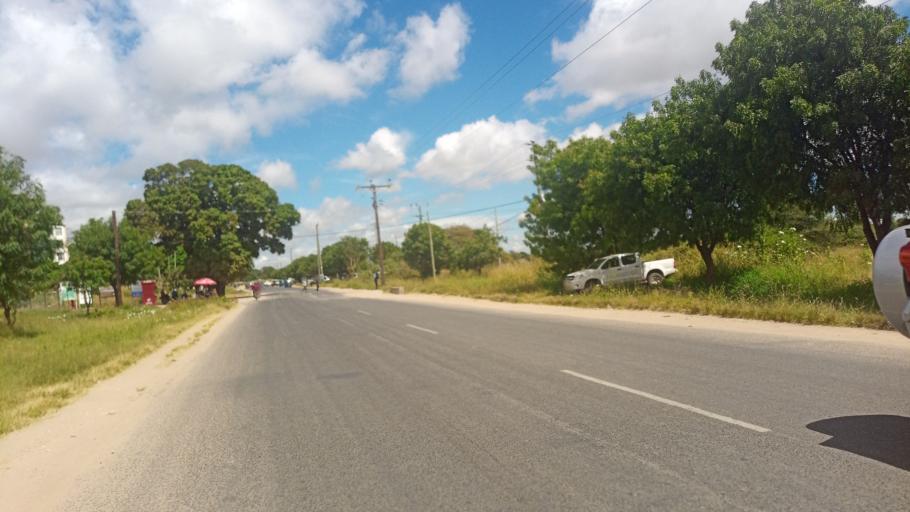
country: TZ
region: Dodoma
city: Dodoma
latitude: -6.1867
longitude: 35.7584
